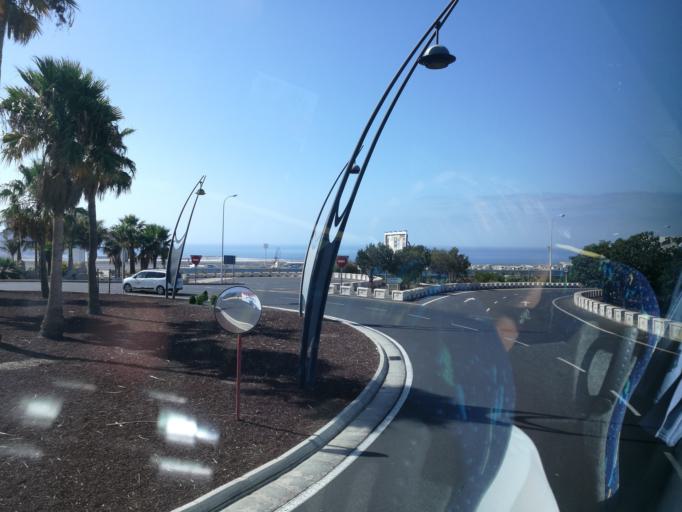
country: ES
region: Canary Islands
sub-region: Provincia de Santa Cruz de Tenerife
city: San Isidro
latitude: 28.0510
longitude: -16.5780
